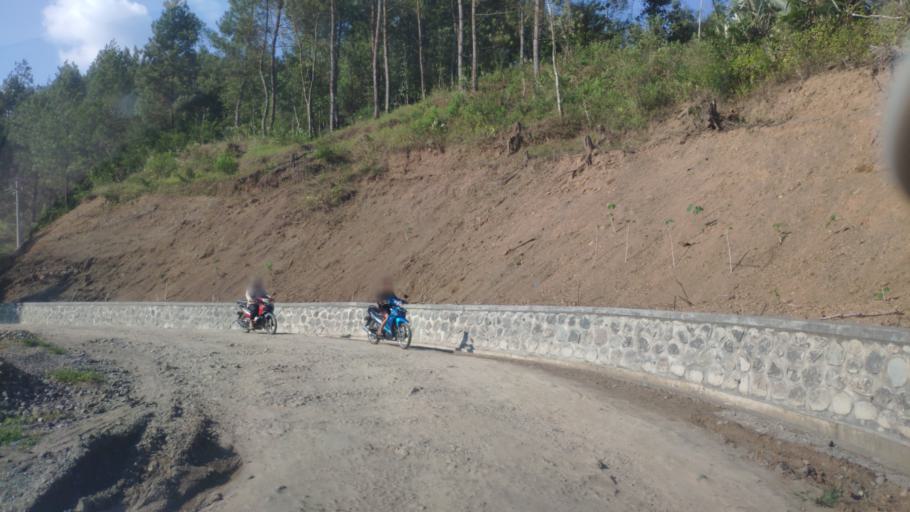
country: ID
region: Central Java
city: Buaran
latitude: -7.2468
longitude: 109.5972
